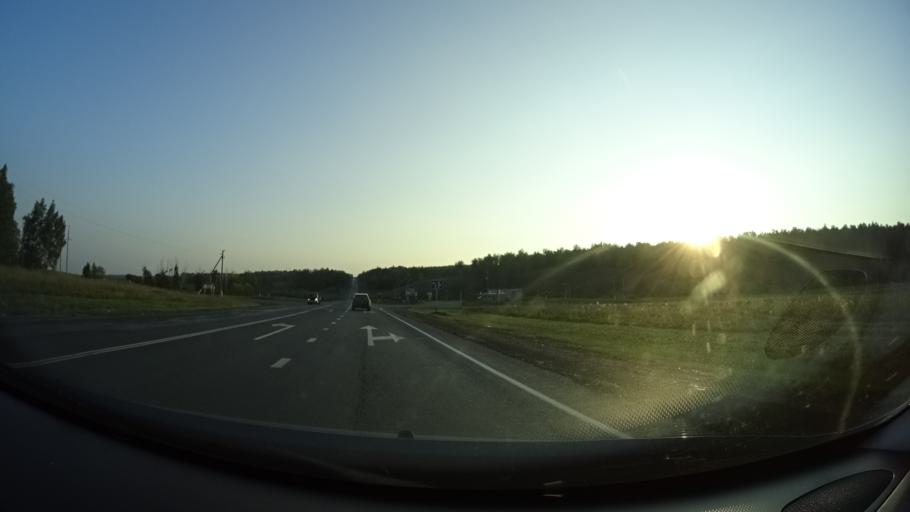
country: RU
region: Samara
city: Isakly
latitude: 54.0017
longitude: 51.5619
